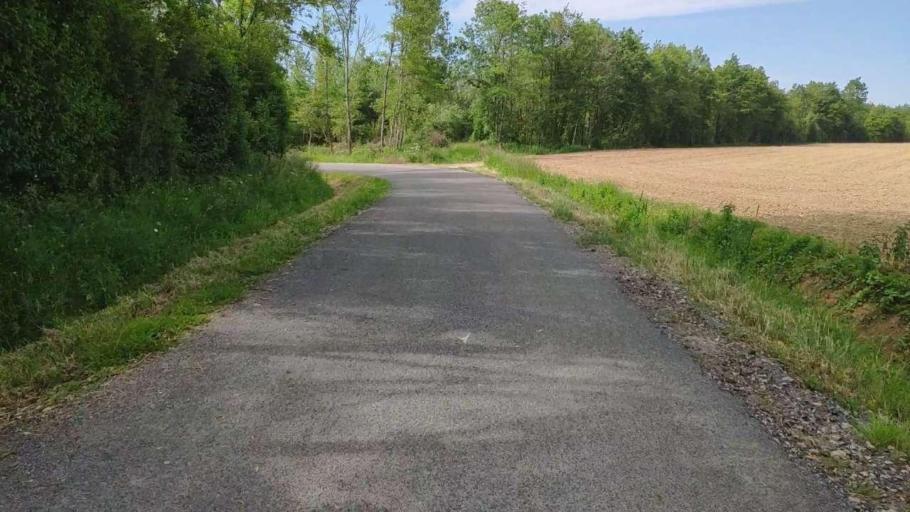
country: FR
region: Franche-Comte
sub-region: Departement du Jura
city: Bletterans
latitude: 46.6802
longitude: 5.4256
